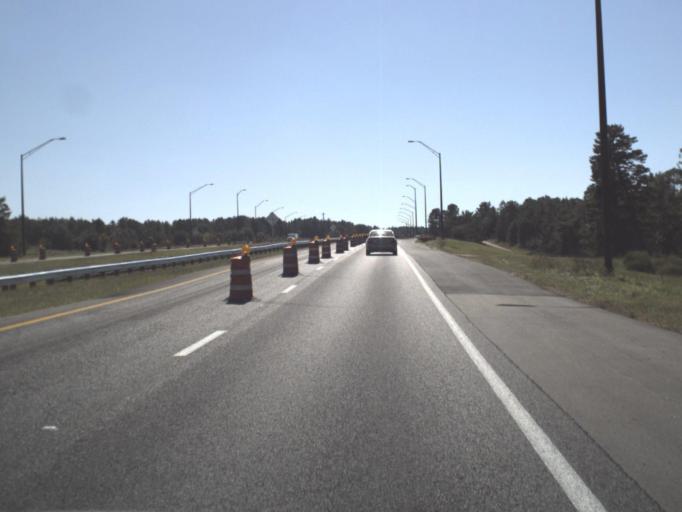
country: US
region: Florida
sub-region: Citrus County
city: Sugarmill Woods
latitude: 28.6724
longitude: -82.4956
